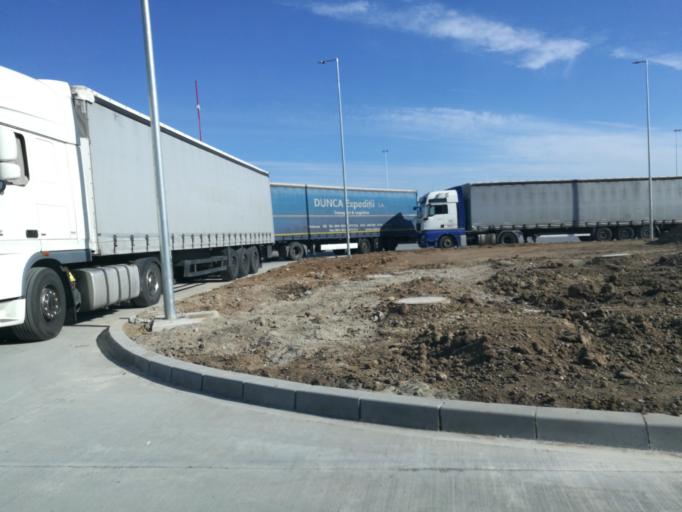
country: RO
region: Giurgiu
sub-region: Comuna Joita
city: Bacu
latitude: 44.4685
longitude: 25.8784
